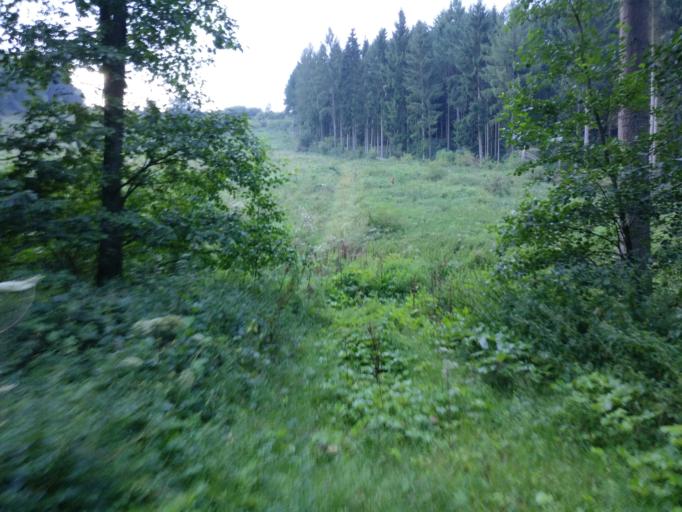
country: DE
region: Hesse
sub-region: Regierungsbezirk Giessen
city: Greifenstein
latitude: 50.6176
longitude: 8.3056
